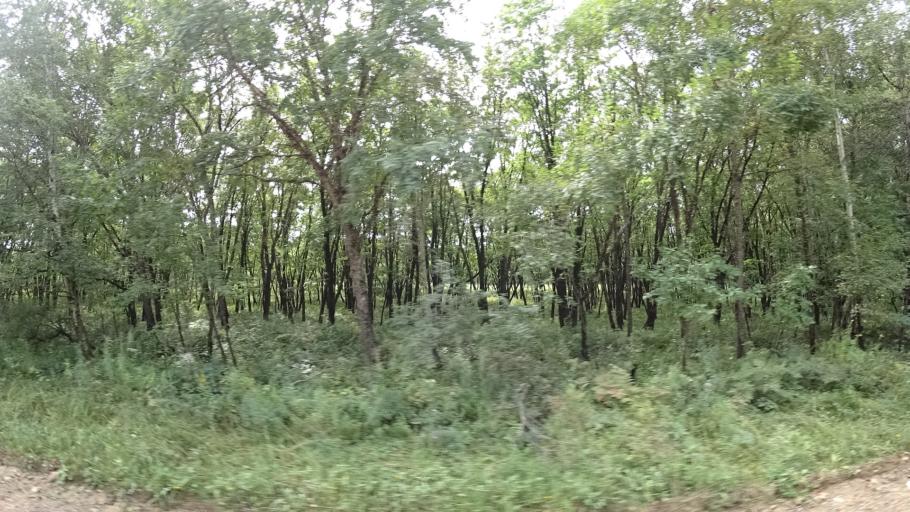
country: RU
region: Primorskiy
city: Lyalichi
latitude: 44.0938
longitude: 132.4322
